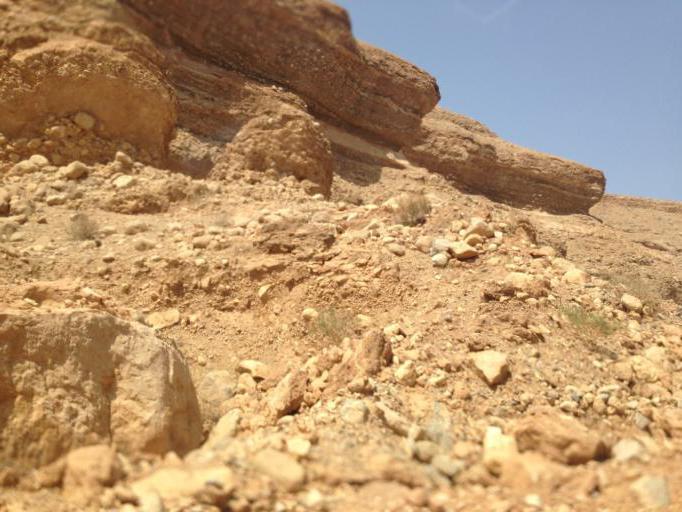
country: OM
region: Ash Sharqiyah
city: Ibra'
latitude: 23.0742
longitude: 58.8823
